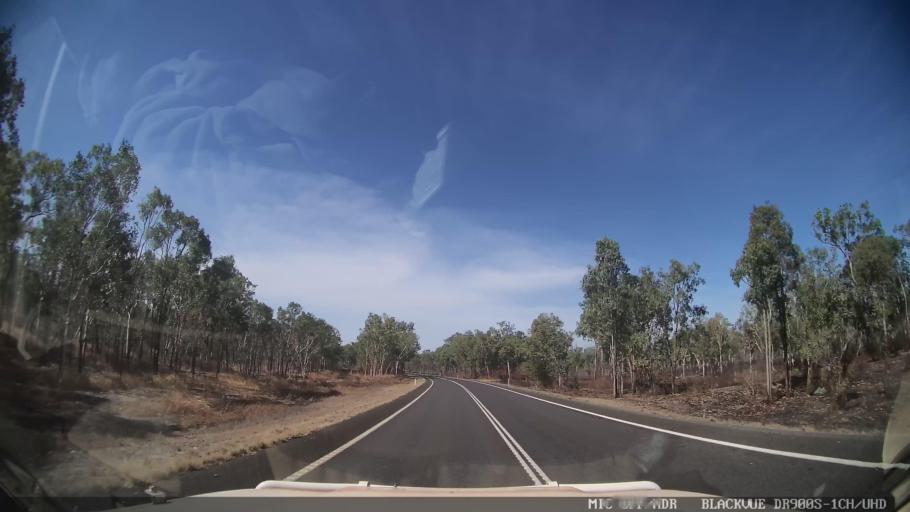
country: AU
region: Queensland
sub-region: Cook
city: Cooktown
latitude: -15.7883
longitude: 144.9506
